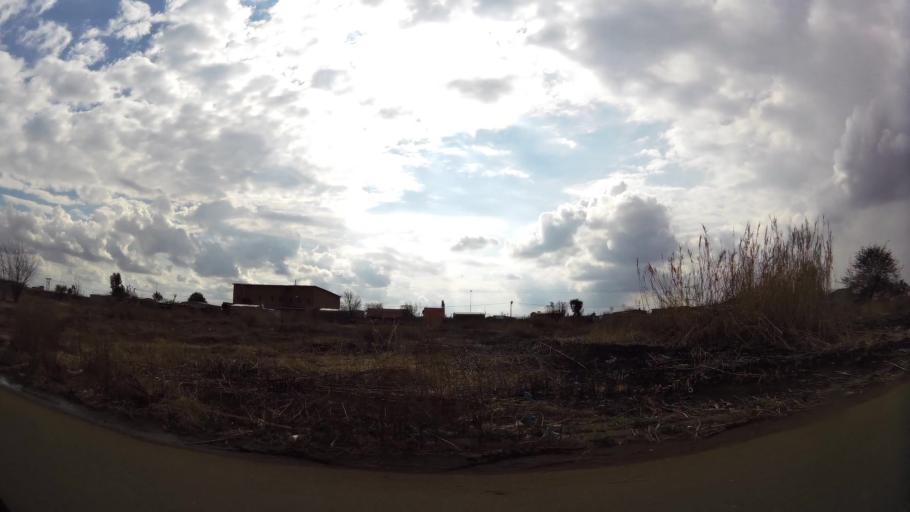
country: ZA
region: Gauteng
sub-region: Sedibeng District Municipality
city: Vanderbijlpark
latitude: -26.7005
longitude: 27.7937
